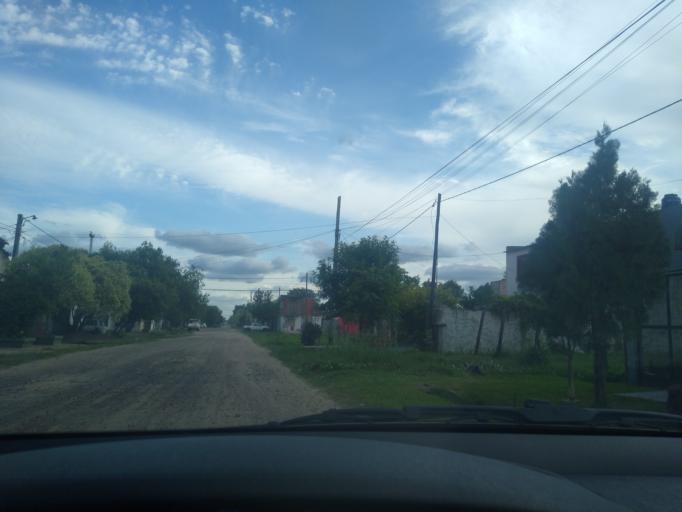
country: AR
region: Chaco
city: Resistencia
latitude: -27.4828
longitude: -58.9694
